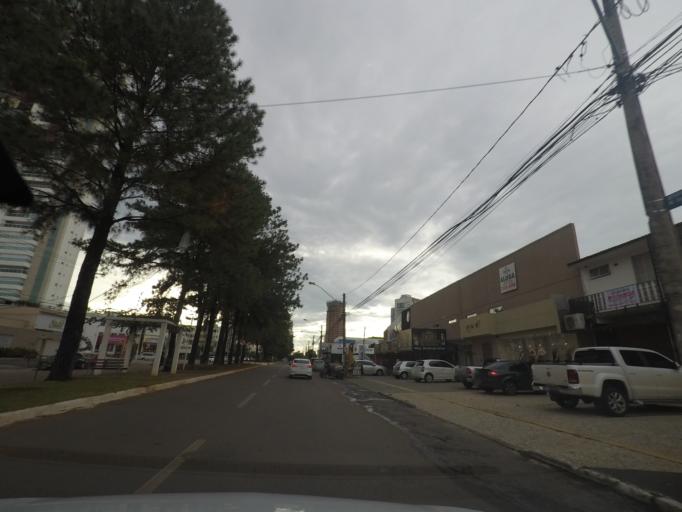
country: BR
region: Goias
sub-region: Goiania
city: Goiania
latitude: -16.7045
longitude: -49.2616
